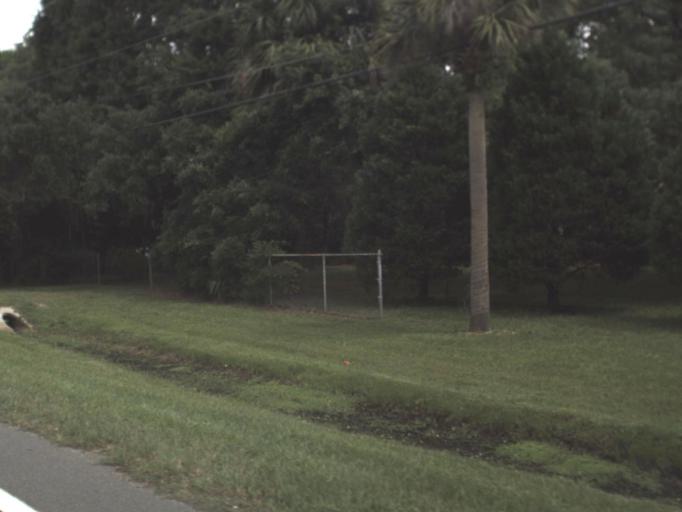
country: US
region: Florida
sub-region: Duval County
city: Atlantic Beach
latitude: 30.4137
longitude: -81.5228
